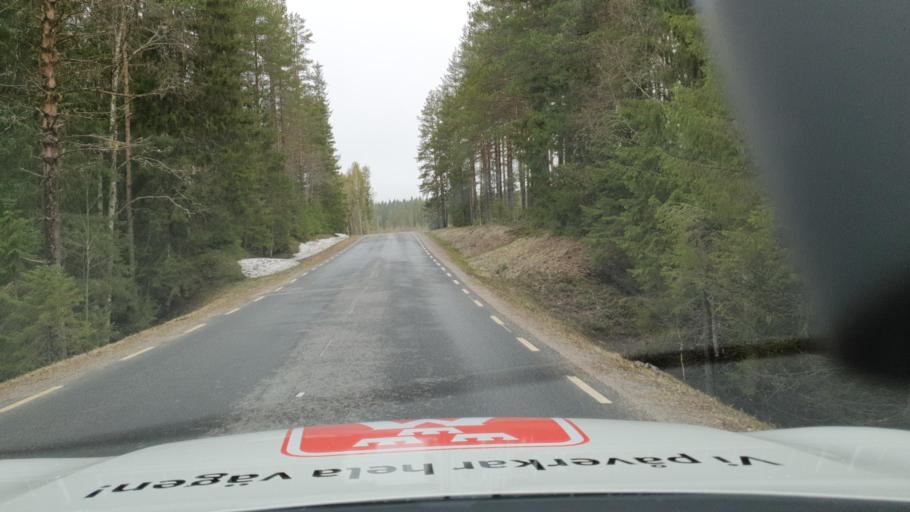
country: SE
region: Vaesterbotten
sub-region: Nordmalings Kommun
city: Nordmaling
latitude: 63.7193
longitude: 19.5643
